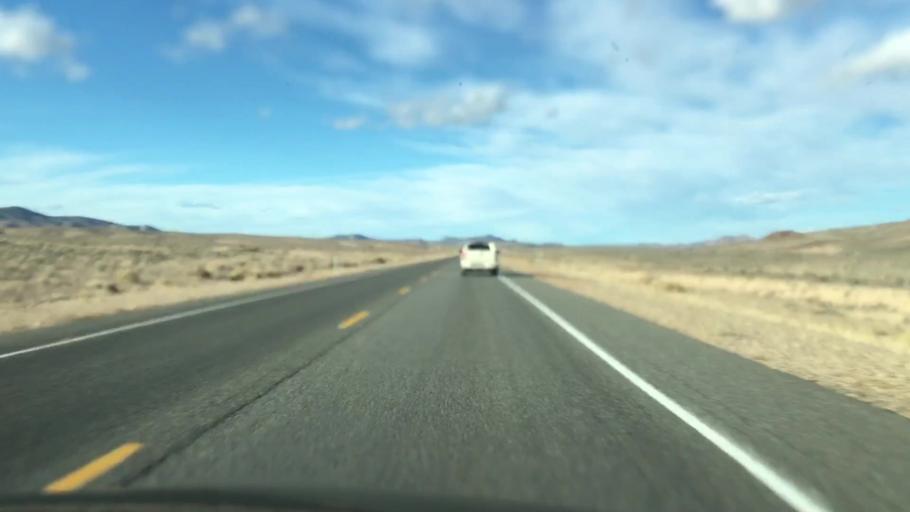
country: US
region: Nevada
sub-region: Esmeralda County
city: Goldfield
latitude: 37.5497
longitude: -117.1968
